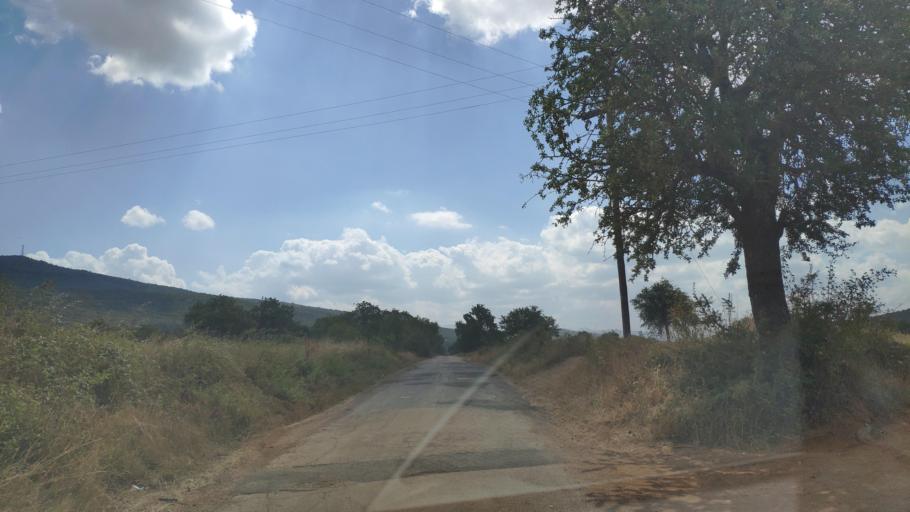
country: GR
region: Peloponnese
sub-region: Nomos Lakonias
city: Kariai
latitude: 37.3175
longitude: 22.4389
